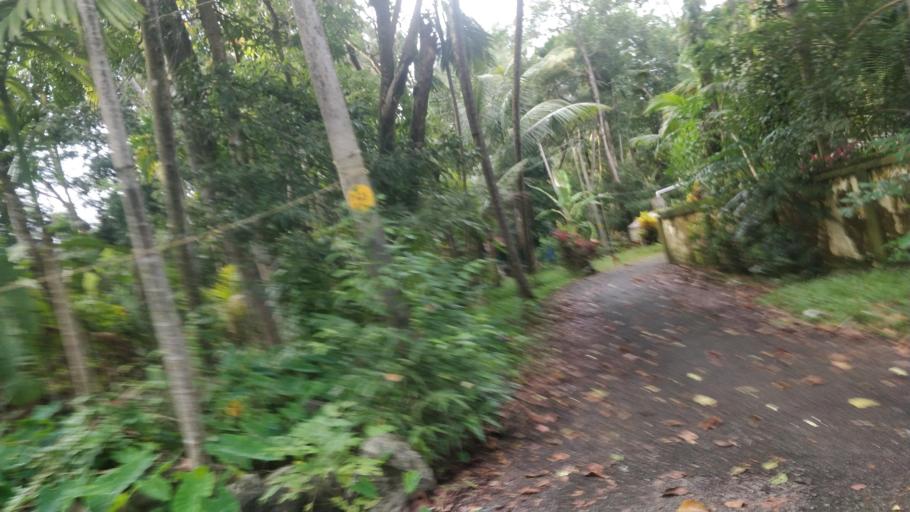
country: IN
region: Kerala
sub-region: Alappuzha
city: Shertallai
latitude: 9.6938
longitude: 76.3643
